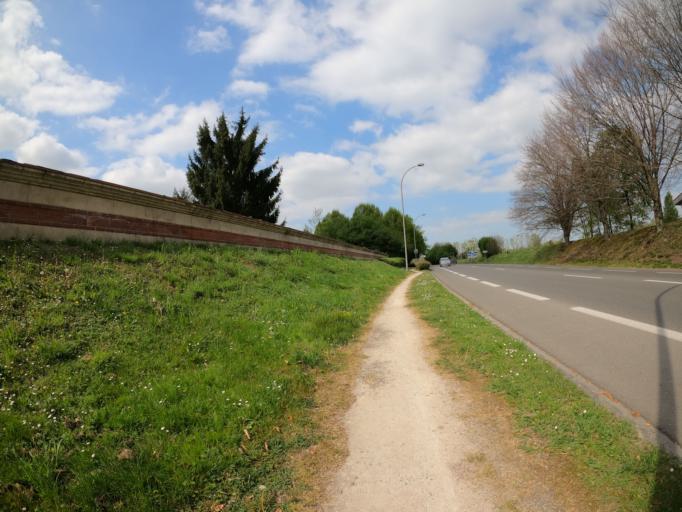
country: FR
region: Aquitaine
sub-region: Departement des Pyrenees-Atlantiques
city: Lons
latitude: 43.3373
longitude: -0.3852
